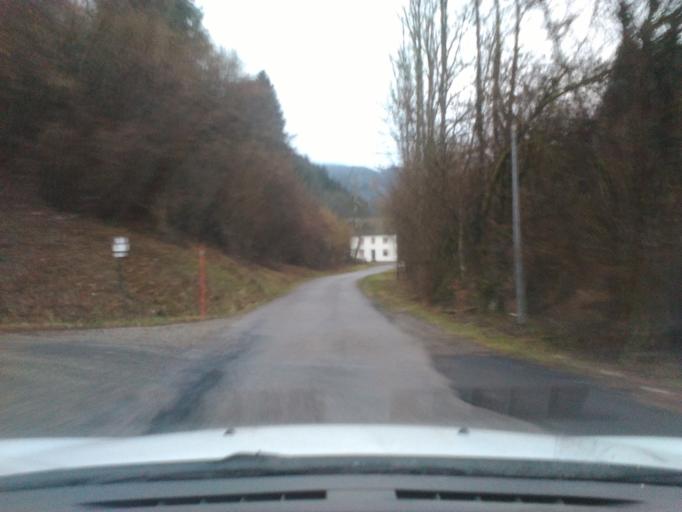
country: FR
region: Lorraine
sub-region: Departement des Vosges
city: La Bresse
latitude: 47.9723
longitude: 6.8654
